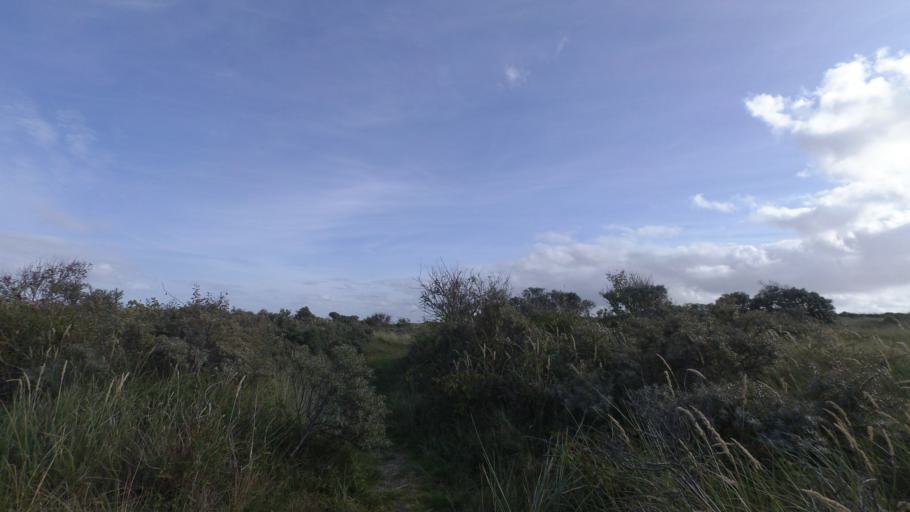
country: NL
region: Friesland
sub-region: Gemeente Ameland
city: Nes
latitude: 53.4574
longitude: 5.8361
